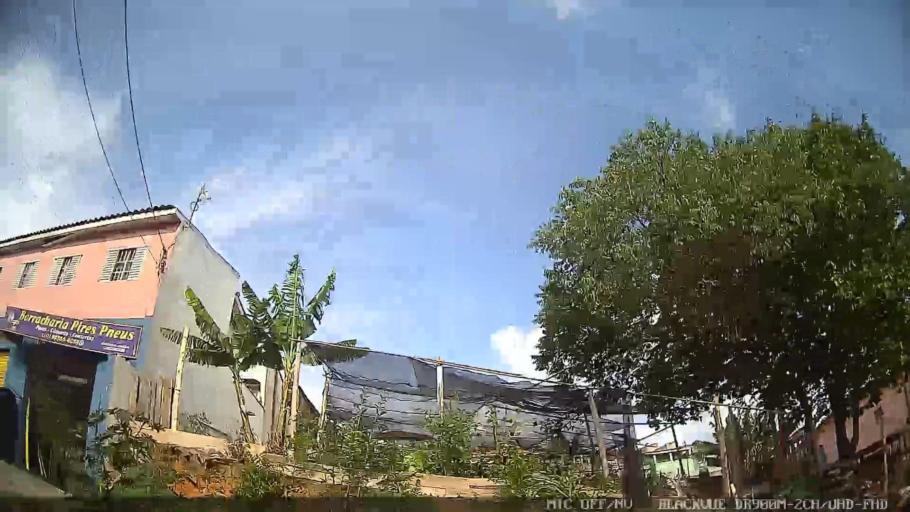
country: BR
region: Sao Paulo
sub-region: Braganca Paulista
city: Braganca Paulista
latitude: -22.9261
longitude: -46.5367
